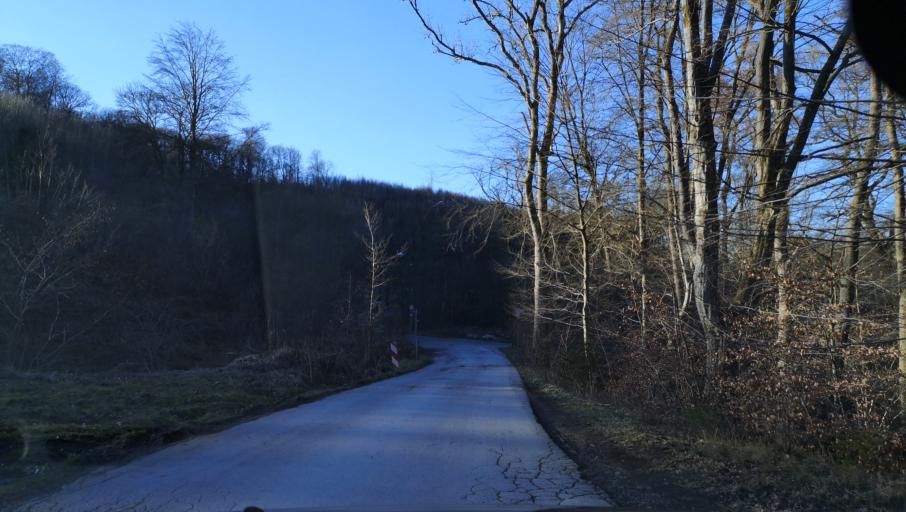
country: DE
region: North Rhine-Westphalia
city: Ennepetal
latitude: 51.2602
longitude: 7.3692
